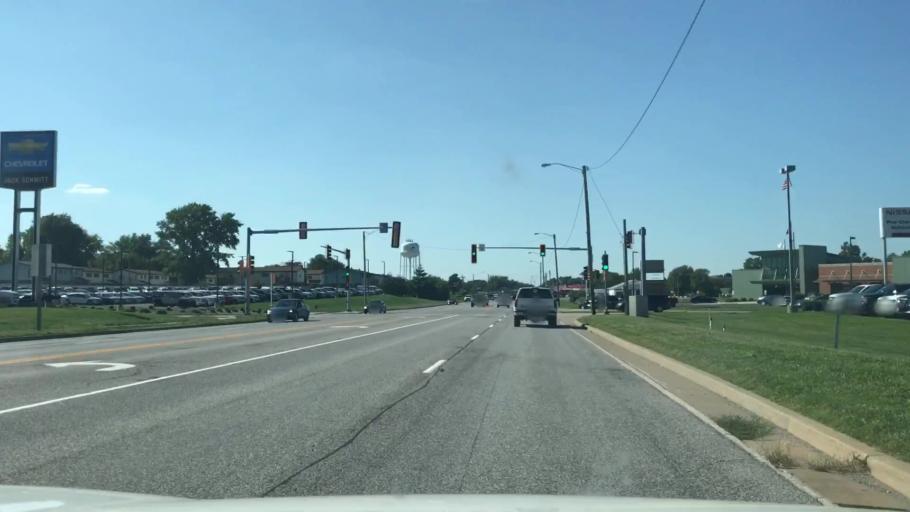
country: US
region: Illinois
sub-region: Madison County
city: Roxana
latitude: 38.8580
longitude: -90.0674
